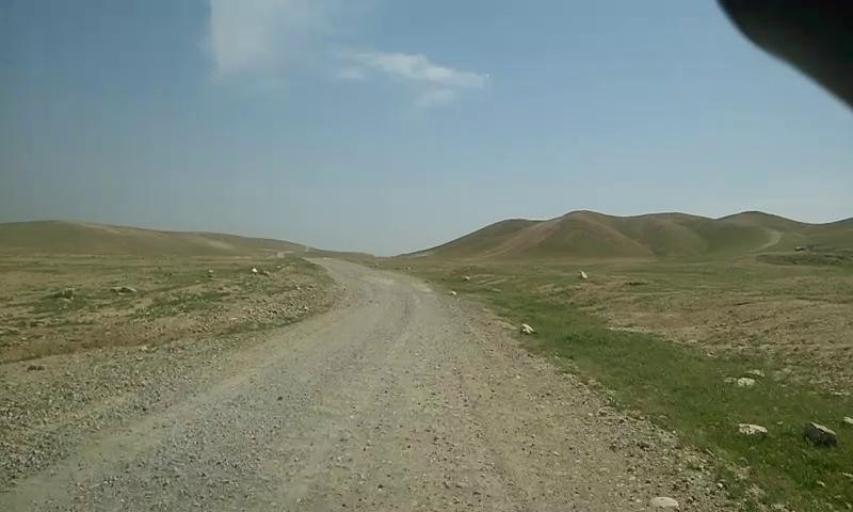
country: PS
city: `Arab ar Rashaydah
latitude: 31.5303
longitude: 35.2875
